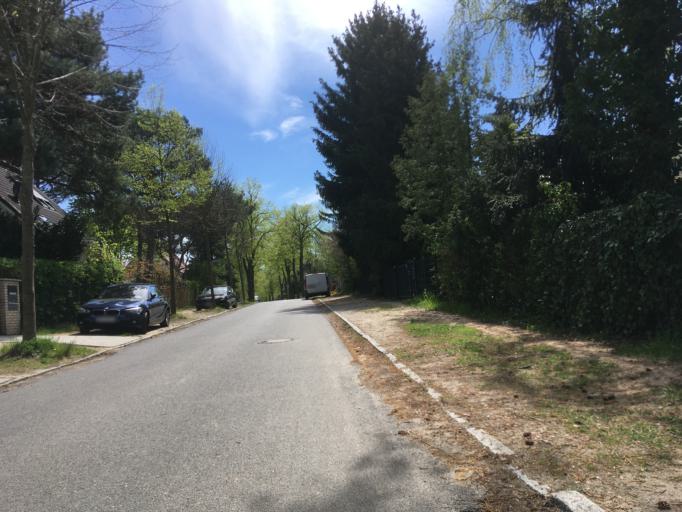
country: DE
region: Brandenburg
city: Zeuthen
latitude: 52.3455
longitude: 13.6068
